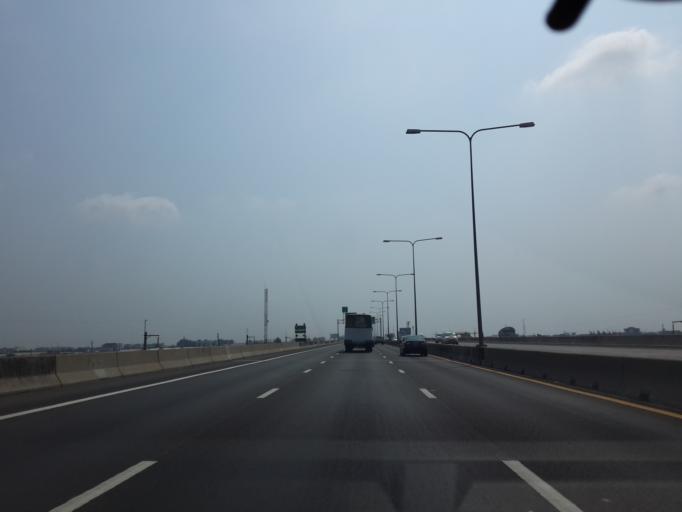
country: TH
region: Samut Prakan
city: Bang Bo District
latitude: 13.5927
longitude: 100.8150
